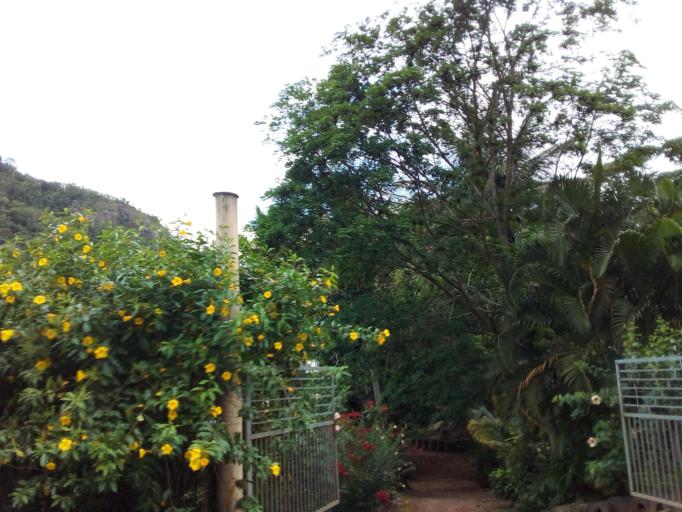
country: BR
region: Espirito Santo
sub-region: Joao Neiva
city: Joao Neiva
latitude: -19.7516
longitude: -40.3667
